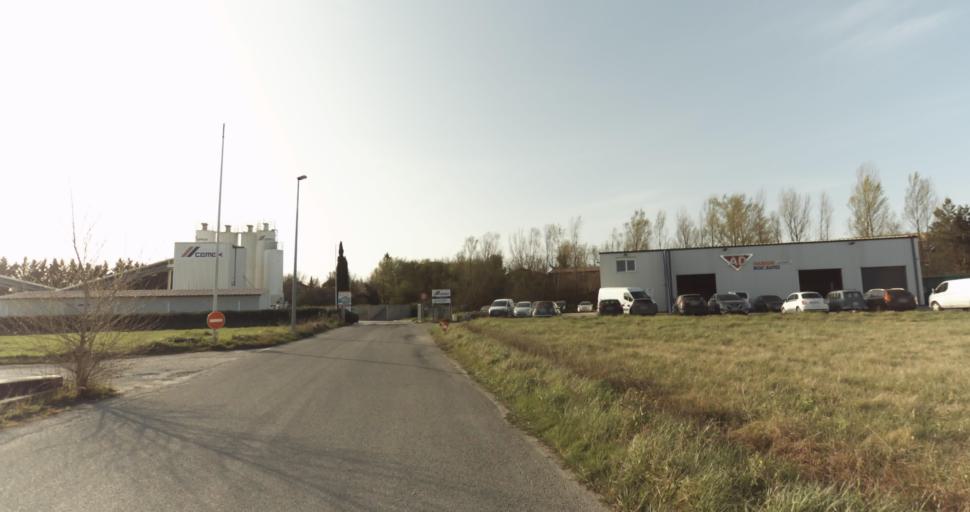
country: FR
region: Midi-Pyrenees
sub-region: Departement du Tarn
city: Saint-Sulpice-la-Pointe
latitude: 43.7680
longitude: 1.6698
